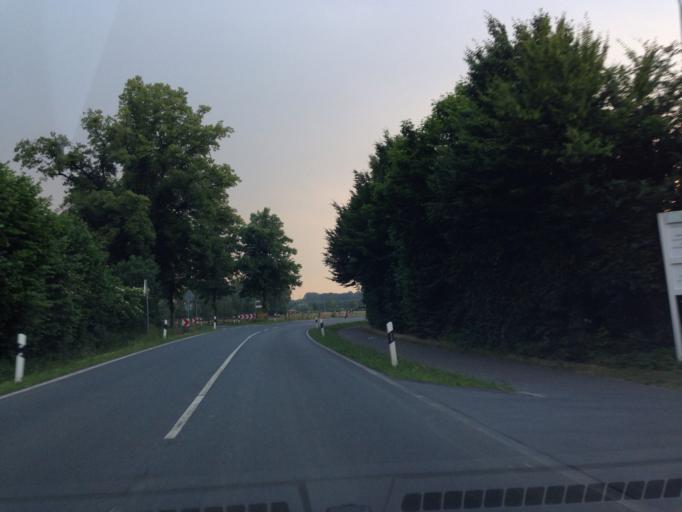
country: DE
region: North Rhine-Westphalia
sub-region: Regierungsbezirk Munster
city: Altenberge
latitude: 51.9642
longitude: 7.5158
